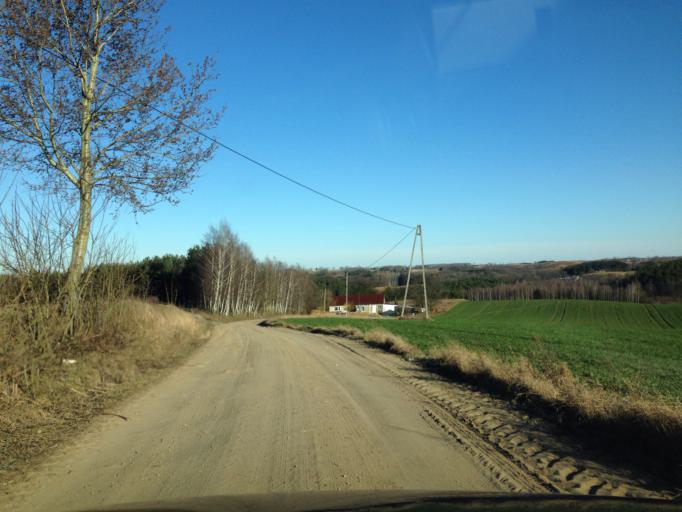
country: PL
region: Kujawsko-Pomorskie
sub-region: Powiat brodnicki
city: Brzozie
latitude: 53.2979
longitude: 19.6590
